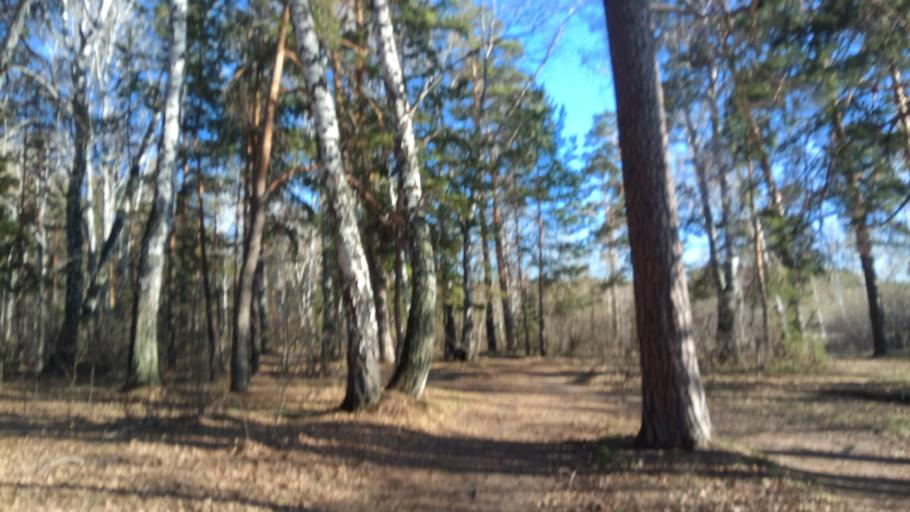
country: RU
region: Chelyabinsk
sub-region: Gorod Chelyabinsk
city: Chelyabinsk
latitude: 55.1425
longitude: 61.3310
